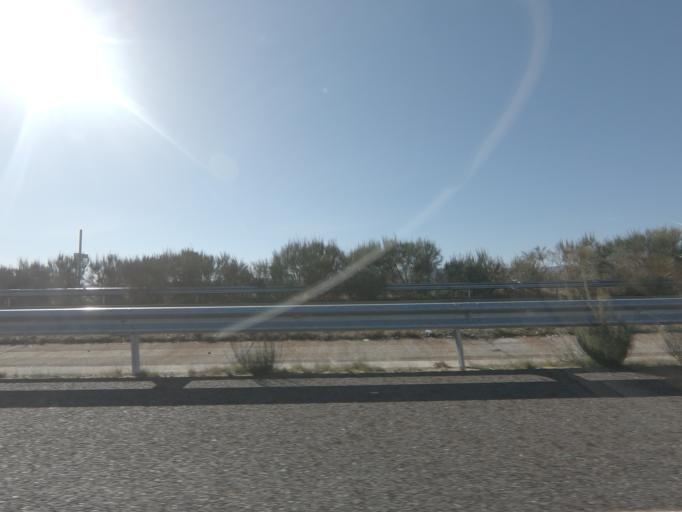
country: ES
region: Galicia
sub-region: Provincia de Ourense
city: Oimbra
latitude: 41.8212
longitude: -7.4187
